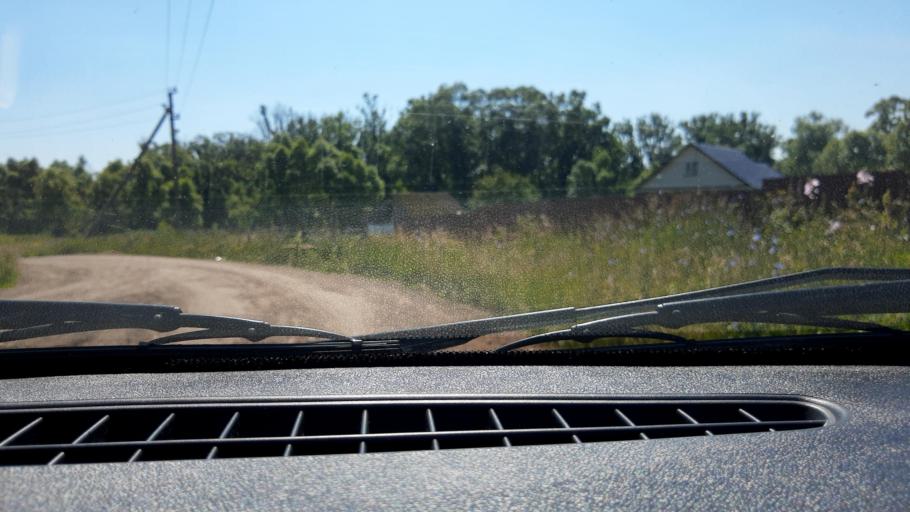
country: RU
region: Bashkortostan
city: Karmaskaly
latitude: 54.3596
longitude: 55.8993
